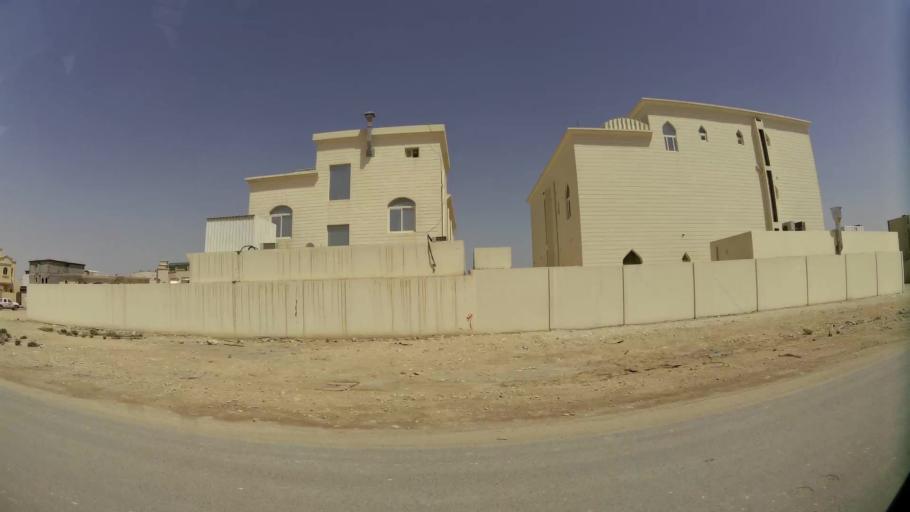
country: QA
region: Baladiyat Umm Salal
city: Umm Salal Muhammad
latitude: 25.3747
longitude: 51.4553
